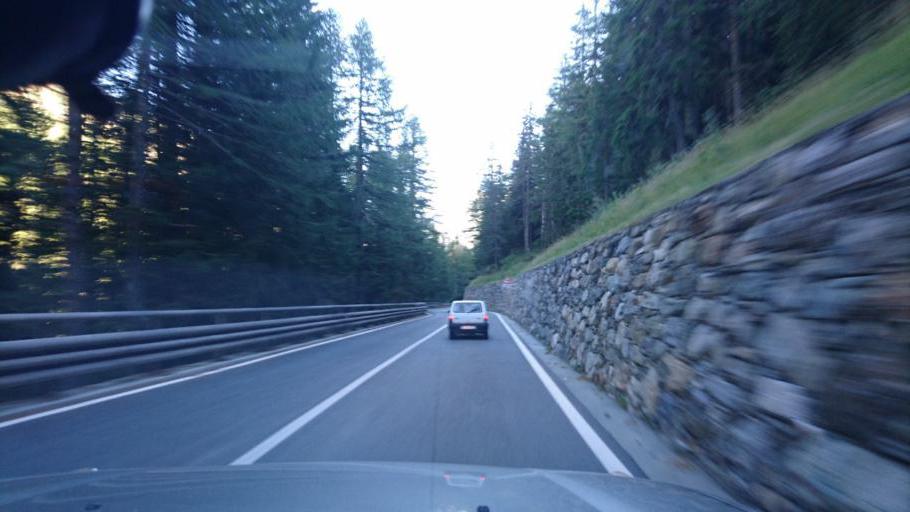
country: IT
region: Aosta Valley
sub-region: Valle d'Aosta
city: San Leonardo
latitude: 45.8423
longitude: 7.1769
